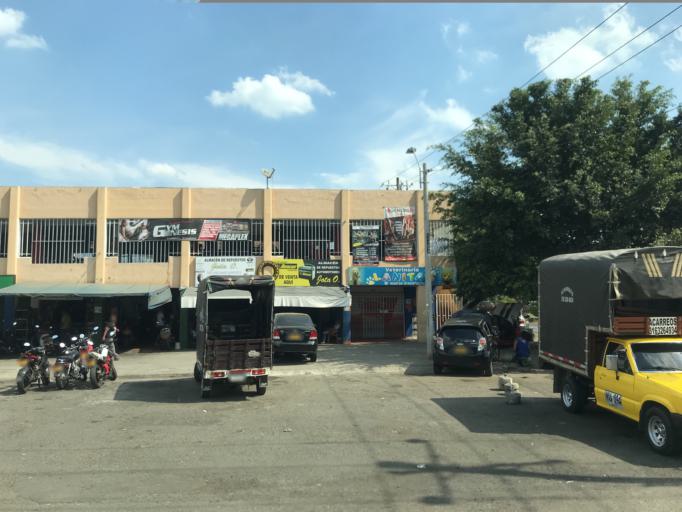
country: CO
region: Valle del Cauca
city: Cali
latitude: 3.4907
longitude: -76.4972
